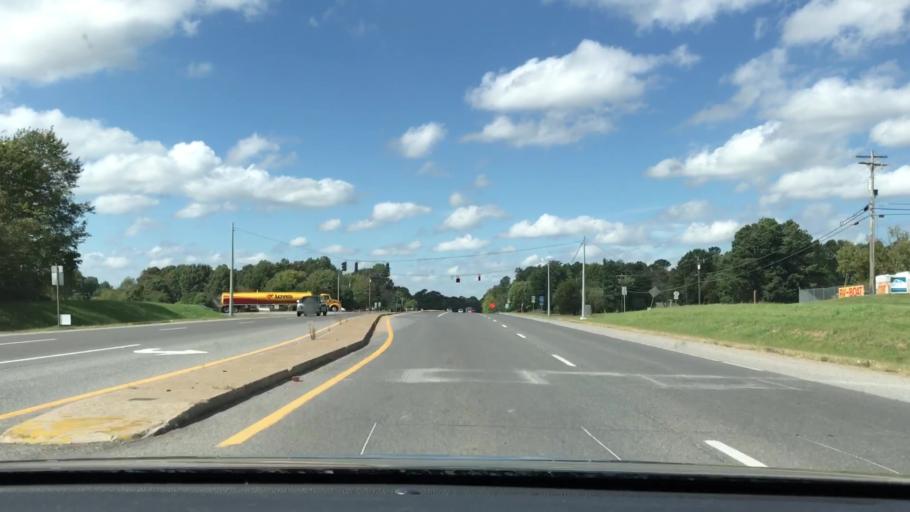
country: US
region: Kentucky
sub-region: McCracken County
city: Reidland
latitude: 37.0092
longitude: -88.5069
